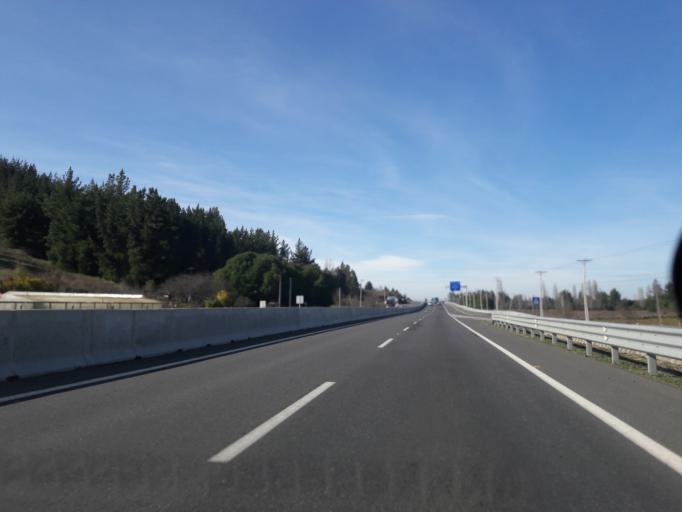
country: CL
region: Biobio
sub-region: Provincia de Biobio
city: Yumbel
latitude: -36.9981
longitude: -72.5767
